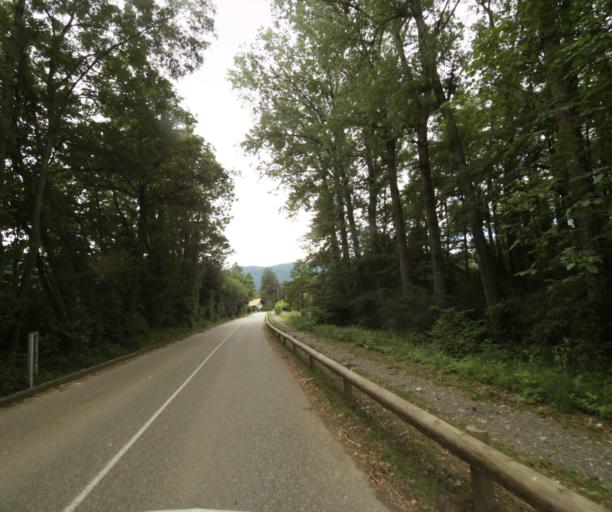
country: FR
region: Rhone-Alpes
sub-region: Departement de la Haute-Savoie
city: Perrignier
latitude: 46.2991
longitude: 6.4207
